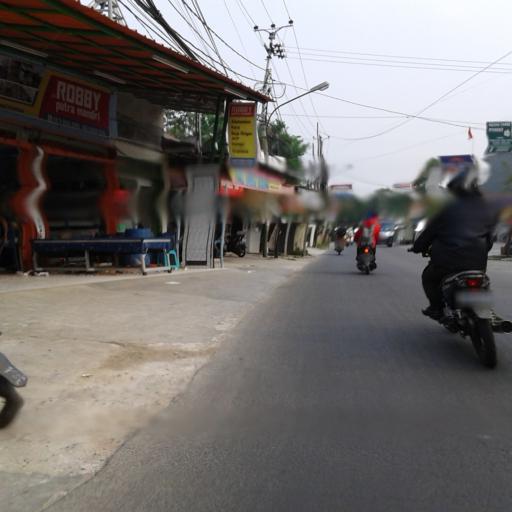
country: ID
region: West Java
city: Sawangan
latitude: -6.3920
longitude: 106.7696
